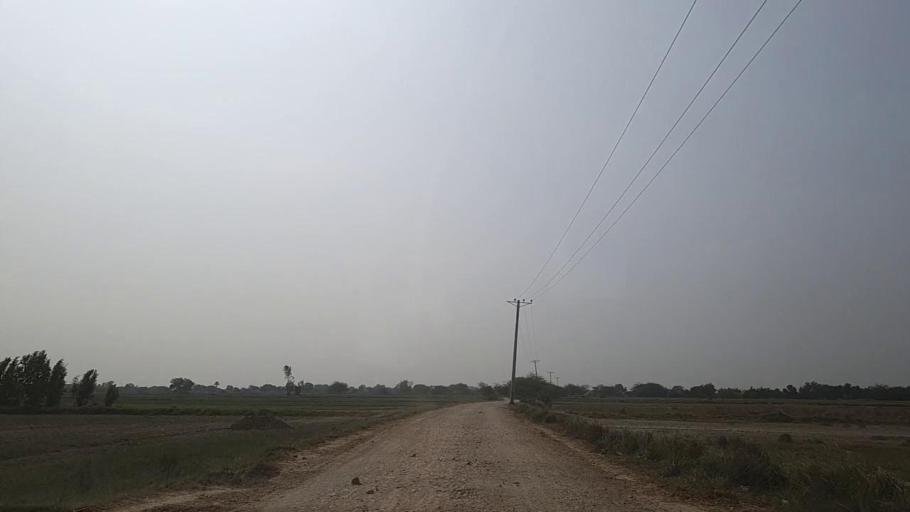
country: PK
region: Sindh
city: Mirpur Sakro
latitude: 24.6117
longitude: 67.7291
